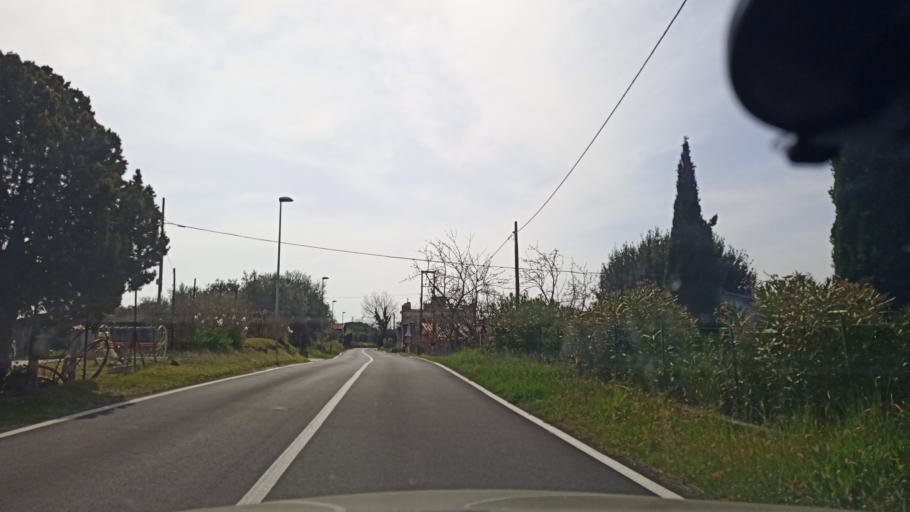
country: IT
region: Latium
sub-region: Provincia di Rieti
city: Torri in Sabina
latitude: 42.3423
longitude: 12.6522
